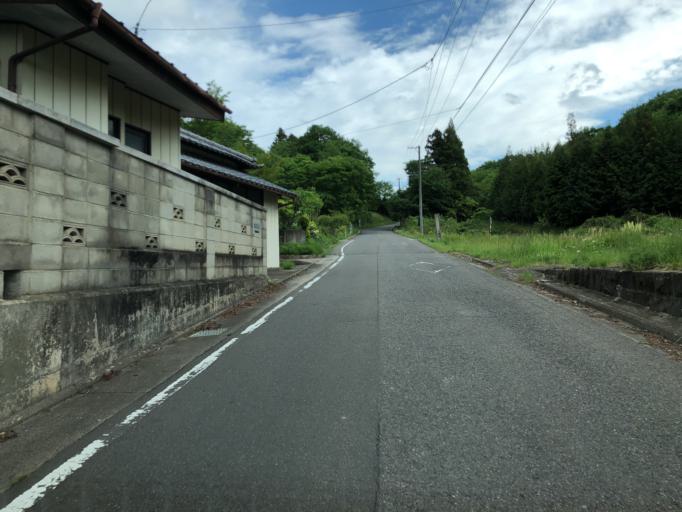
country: JP
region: Fukushima
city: Nihommatsu
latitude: 37.6374
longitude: 140.5017
